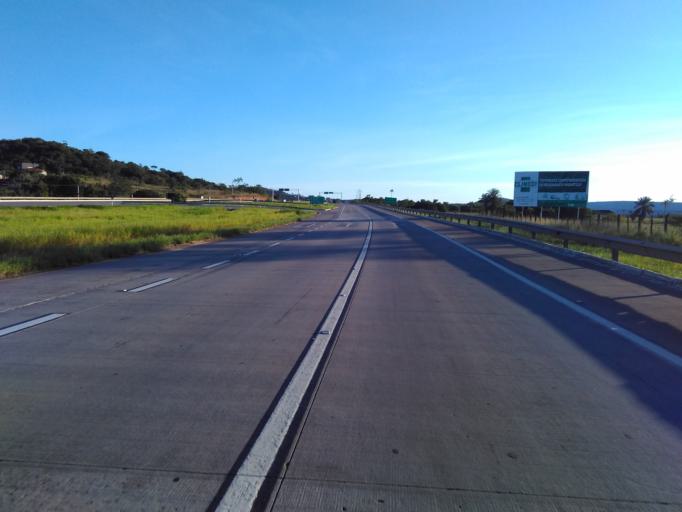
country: BR
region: Sergipe
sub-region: Nossa Senhora Do Socorro
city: Nossa Senhora do Socorro
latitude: -10.9176
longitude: -37.1675
